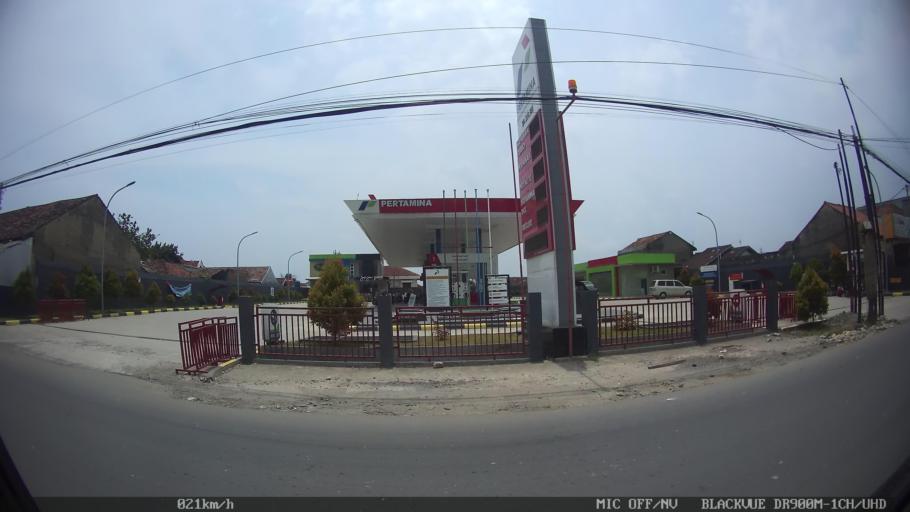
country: ID
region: Lampung
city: Kedaton
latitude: -5.3954
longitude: 105.2981
